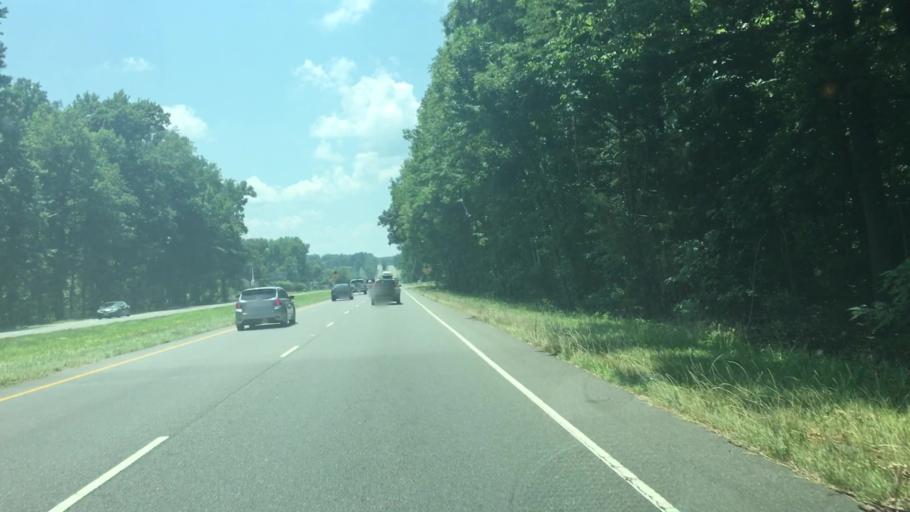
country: US
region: Virginia
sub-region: King George County
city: Dahlgren
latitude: 38.3445
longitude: -77.0657
